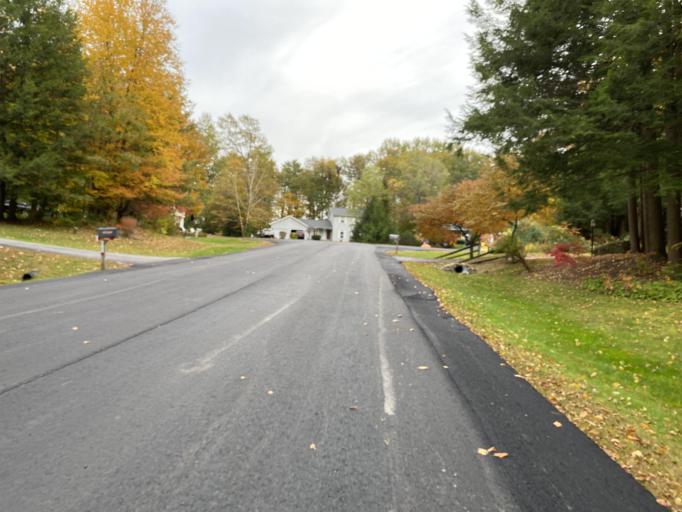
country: US
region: New York
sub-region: Saratoga County
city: Milton
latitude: 43.0949
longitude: -73.9046
